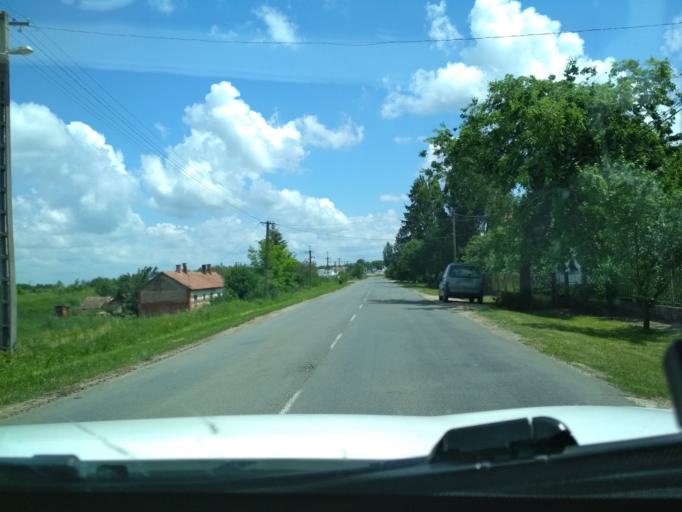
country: HU
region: Jasz-Nagykun-Szolnok
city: Tiszafured
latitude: 47.6124
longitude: 20.7780
